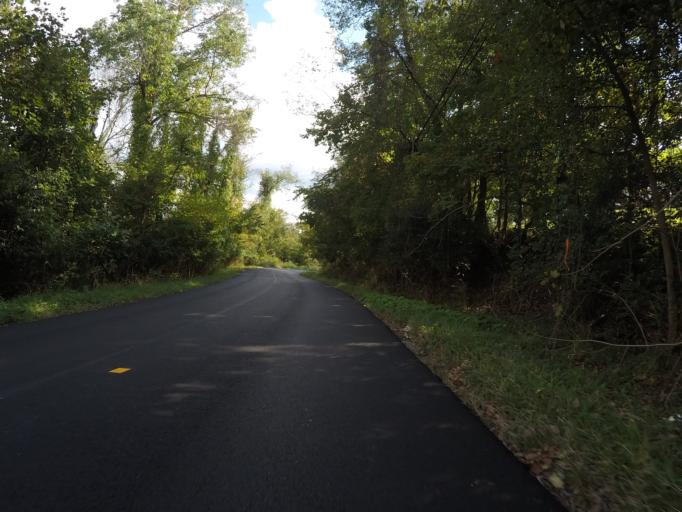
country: US
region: West Virginia
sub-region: Cabell County
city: Huntington
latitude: 38.3841
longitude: -82.4274
